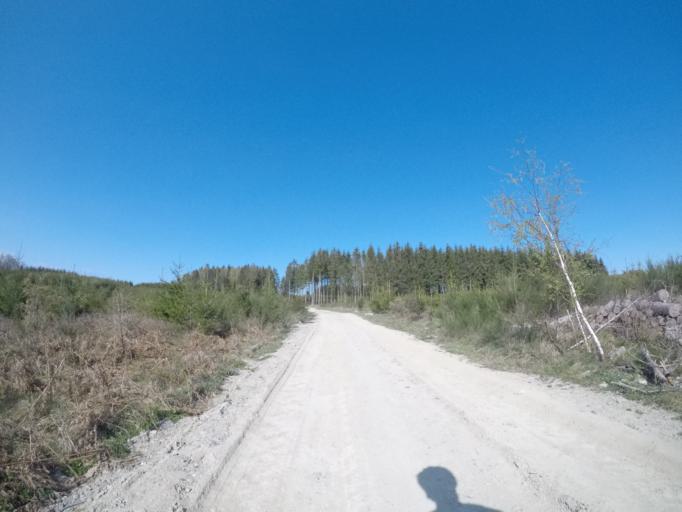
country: BE
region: Wallonia
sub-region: Province du Luxembourg
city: Leglise
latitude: 49.7888
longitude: 5.5871
